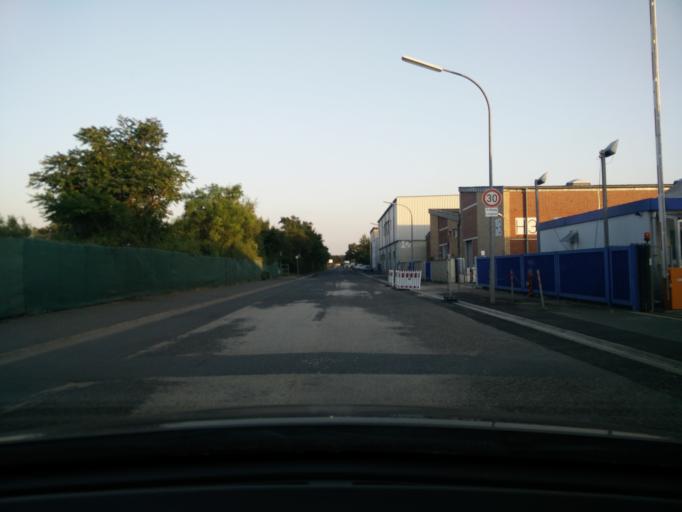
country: DE
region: Bavaria
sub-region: Regierungsbezirk Mittelfranken
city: Nuernberg
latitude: 49.4249
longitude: 11.0976
